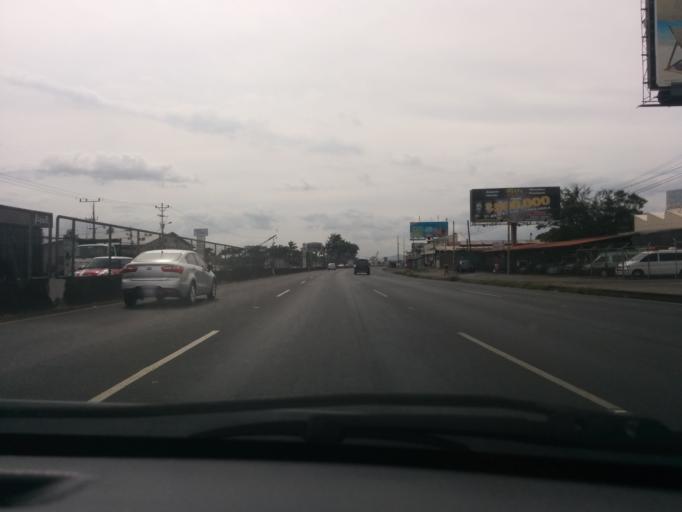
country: CR
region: Heredia
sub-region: Canton de Belen
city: San Antonio
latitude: 10.0009
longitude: -84.1863
